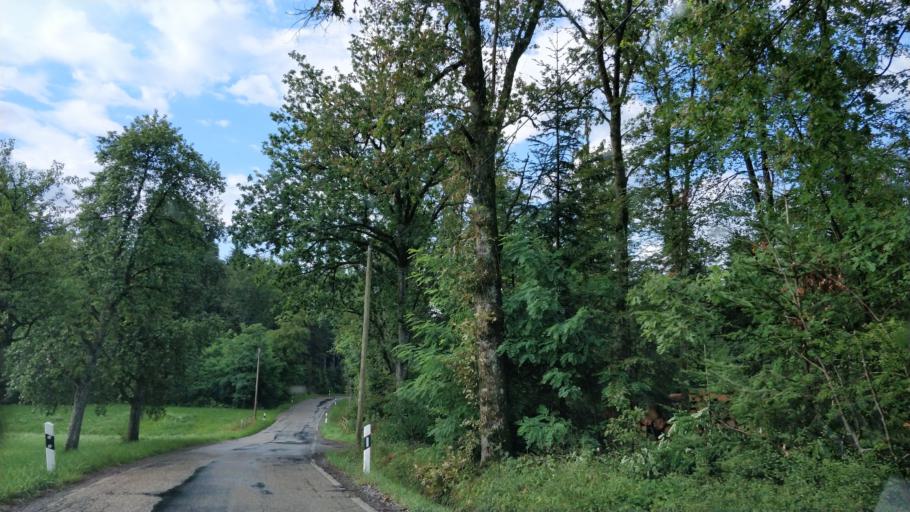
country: DE
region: Baden-Wuerttemberg
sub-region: Regierungsbezirk Stuttgart
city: Fichtenberg
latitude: 48.9738
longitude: 9.6795
